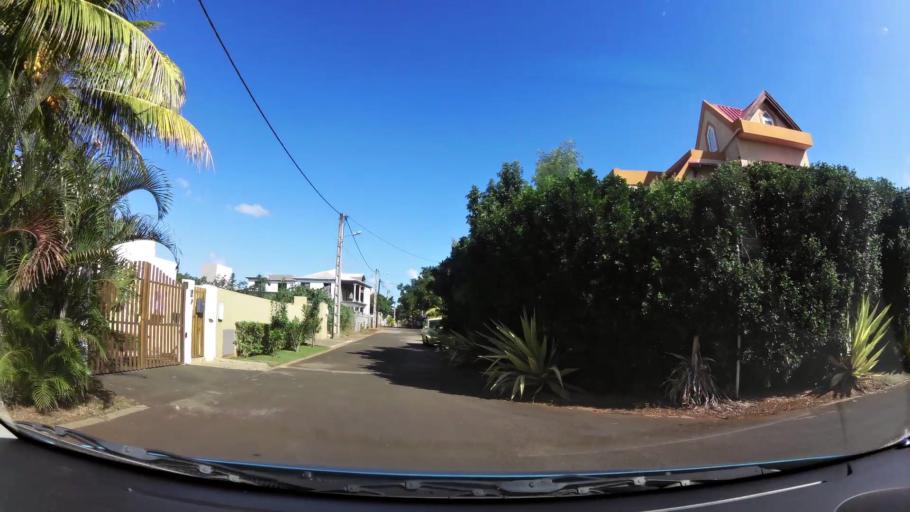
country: MU
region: Black River
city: Albion
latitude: -20.2246
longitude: 57.4154
